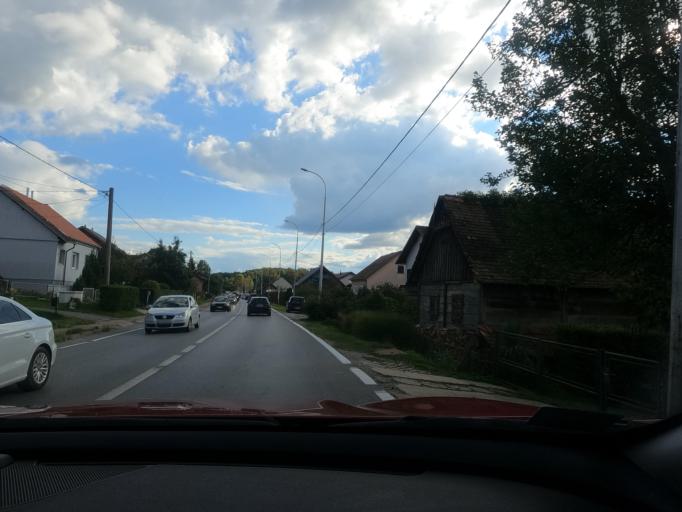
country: HR
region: Sisacko-Moslavacka
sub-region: Grad Sisak
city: Sisak
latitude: 45.4464
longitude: 16.3681
